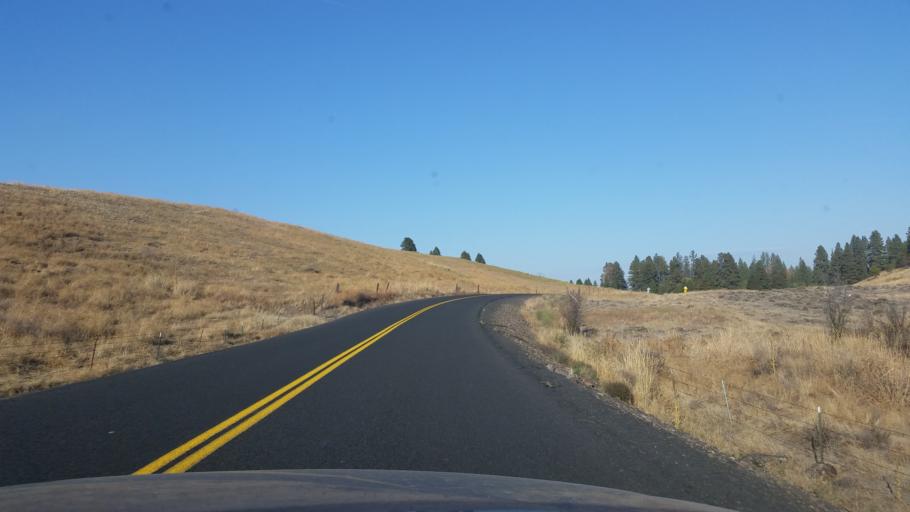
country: US
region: Washington
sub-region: Spokane County
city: Cheney
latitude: 47.3583
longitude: -117.7039
